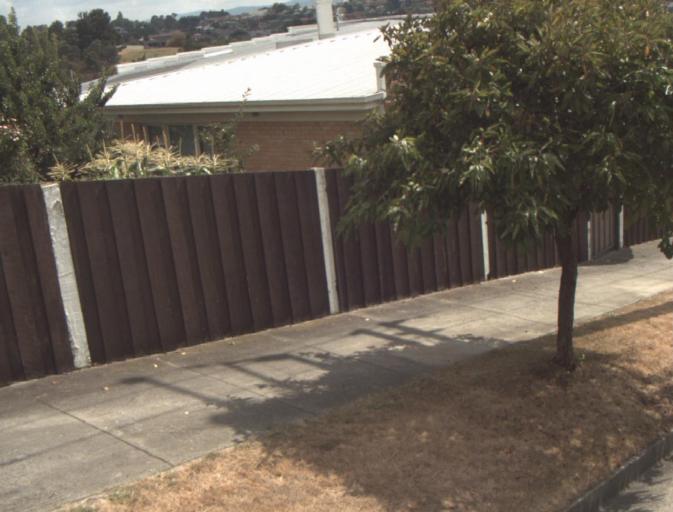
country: AU
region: Tasmania
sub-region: Launceston
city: Summerhill
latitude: -41.4675
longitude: 147.1540
